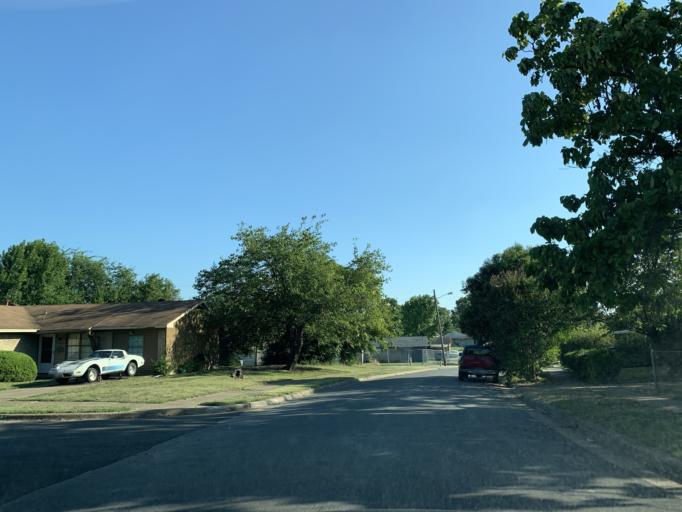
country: US
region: Texas
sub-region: Dallas County
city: Hutchins
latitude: 32.6619
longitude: -96.7661
